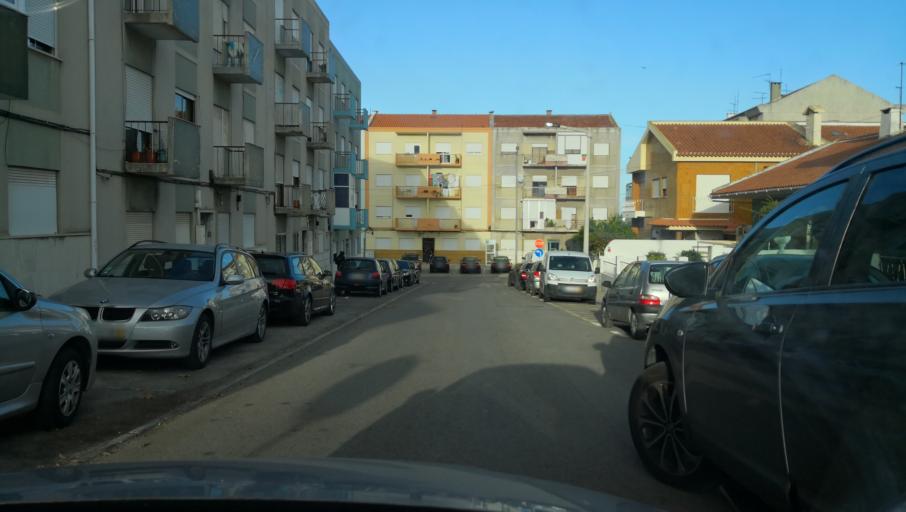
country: PT
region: Setubal
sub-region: Barreiro
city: Barreiro
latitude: 38.6689
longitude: -9.0487
